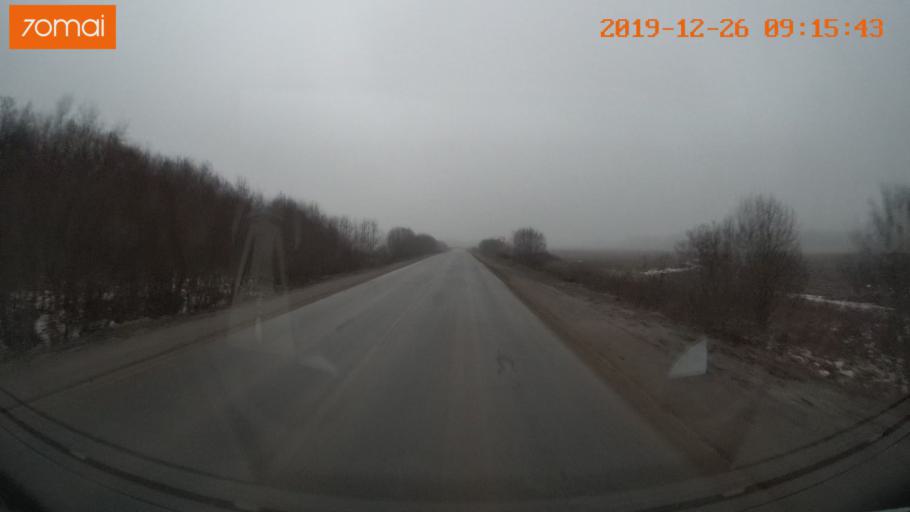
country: RU
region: Vologda
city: Gryazovets
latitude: 58.9086
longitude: 40.2398
